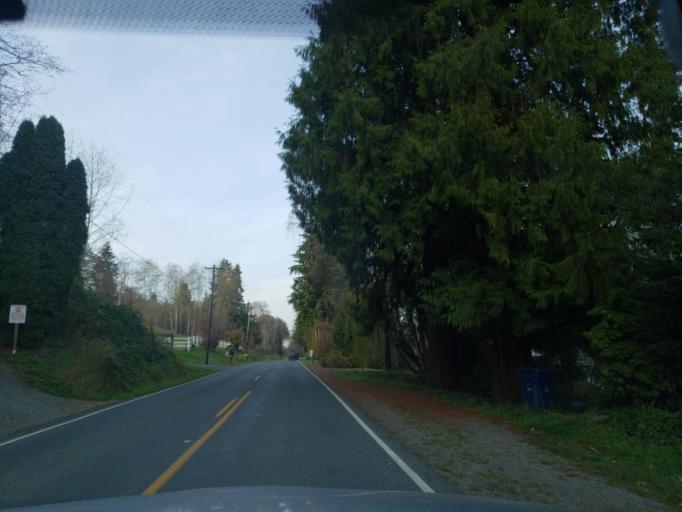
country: US
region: Washington
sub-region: Snohomish County
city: Cathcart
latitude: 47.8496
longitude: -122.0929
